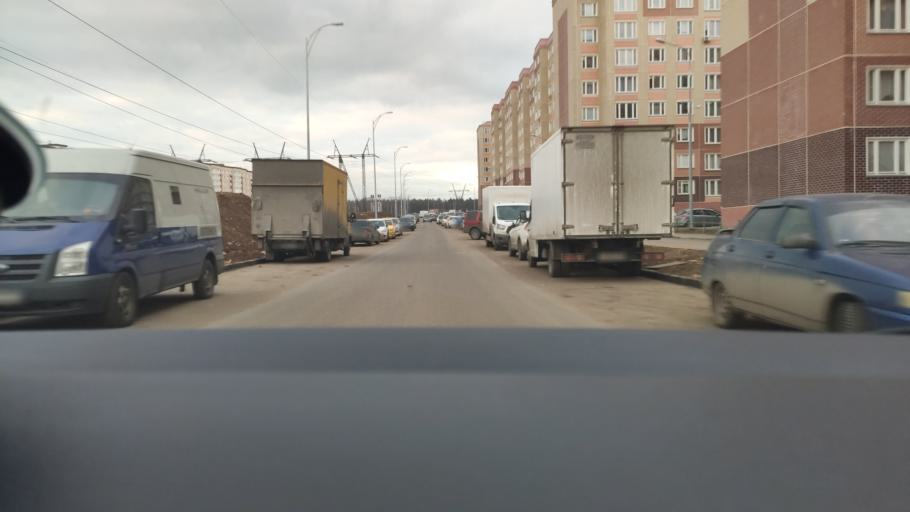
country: RU
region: Moscow
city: Zagor'ye
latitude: 55.5328
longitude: 37.6390
